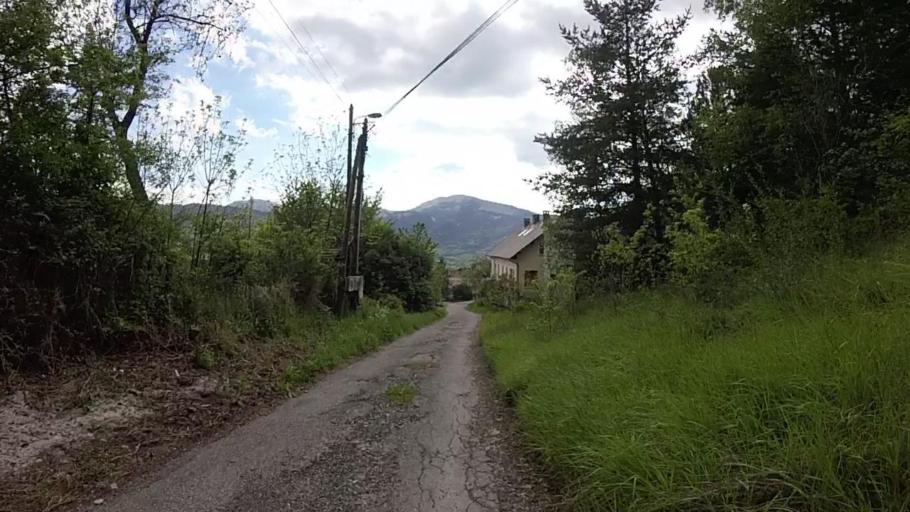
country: FR
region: Provence-Alpes-Cote d'Azur
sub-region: Departement des Alpes-de-Haute-Provence
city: Seyne-les-Alpes
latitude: 44.3512
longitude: 6.3630
